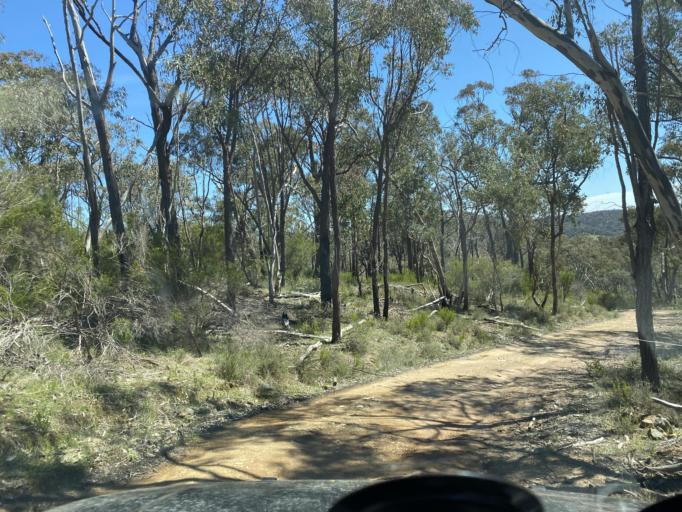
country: AU
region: Victoria
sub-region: Benalla
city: Benalla
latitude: -36.6981
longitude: 146.1517
